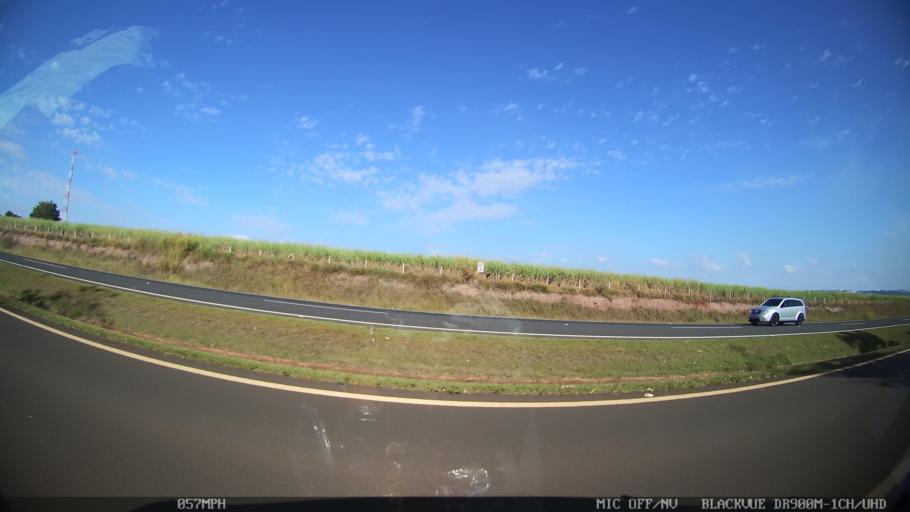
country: BR
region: Sao Paulo
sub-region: Iracemapolis
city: Iracemapolis
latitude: -22.6705
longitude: -47.5543
